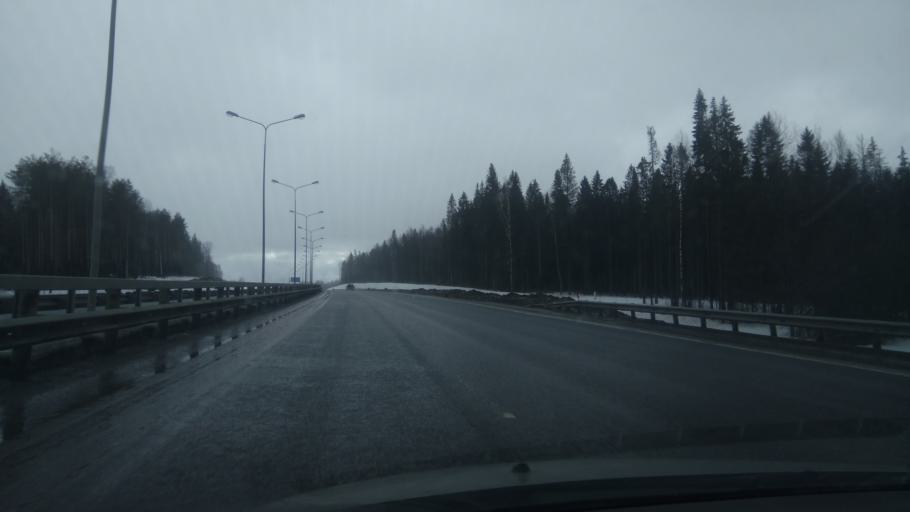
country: RU
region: Perm
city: Zvezdnyy
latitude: 57.7455
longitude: 56.3353
